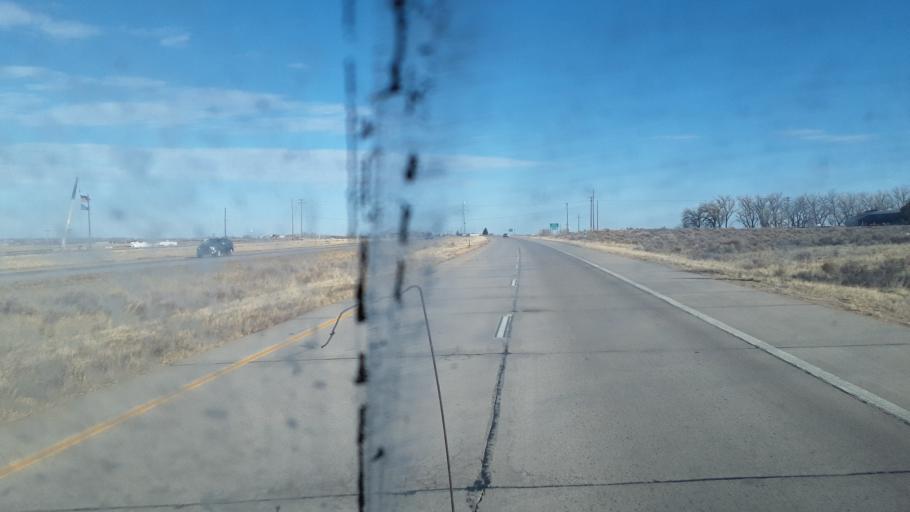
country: US
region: Colorado
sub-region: Morgan County
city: Fort Morgan
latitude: 40.2433
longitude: -103.9086
